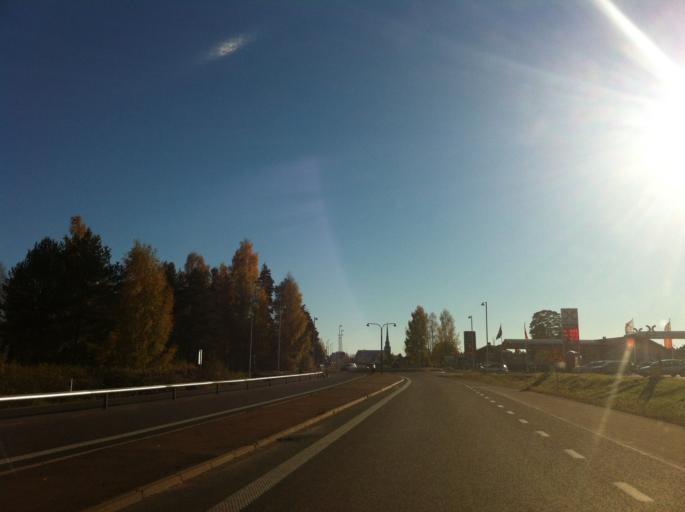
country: SE
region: Dalarna
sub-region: Mora Kommun
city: Mora
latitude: 61.0174
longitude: 14.5387
